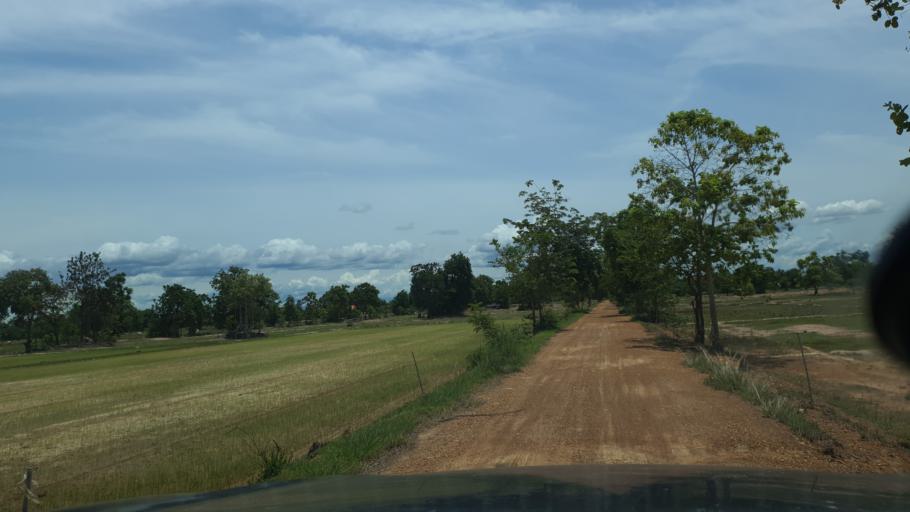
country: TH
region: Sukhothai
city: Ban Na
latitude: 17.1462
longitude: 99.6685
